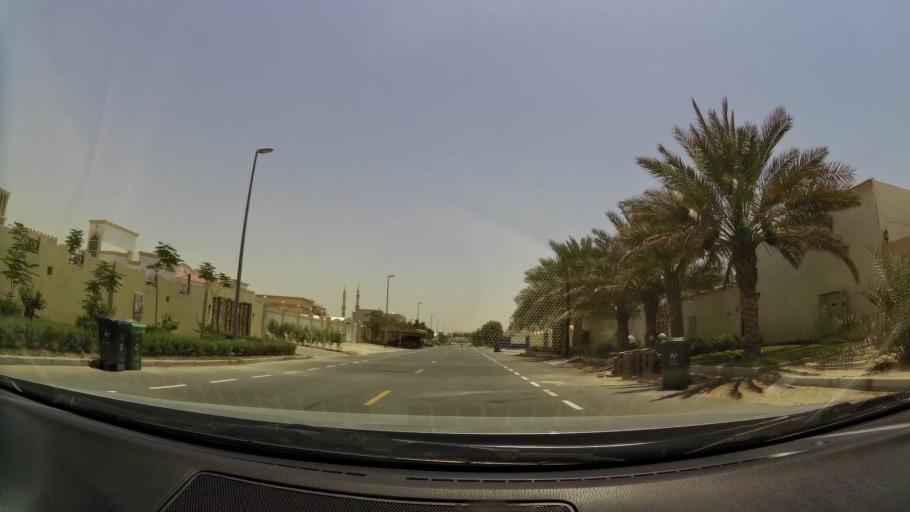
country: AE
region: Dubai
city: Dubai
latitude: 25.0959
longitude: 55.2000
